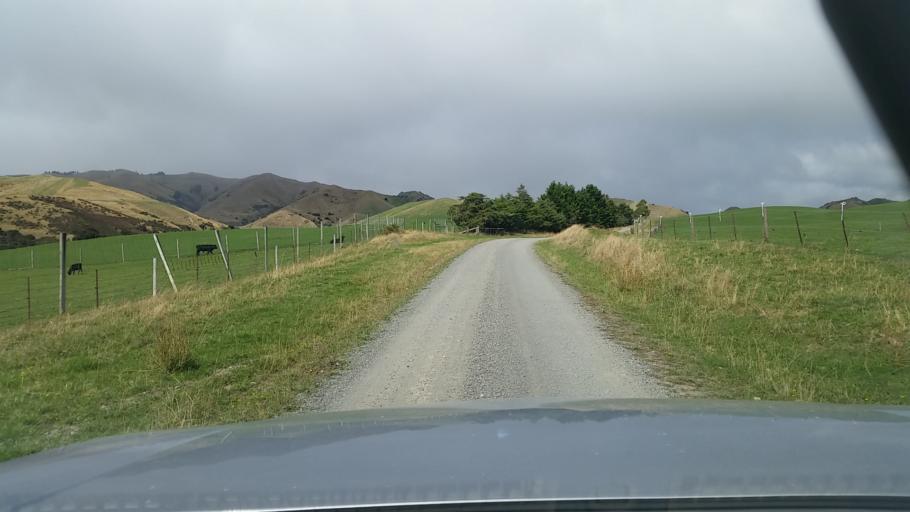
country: NZ
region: Marlborough
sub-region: Marlborough District
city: Blenheim
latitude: -41.7489
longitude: 173.8958
